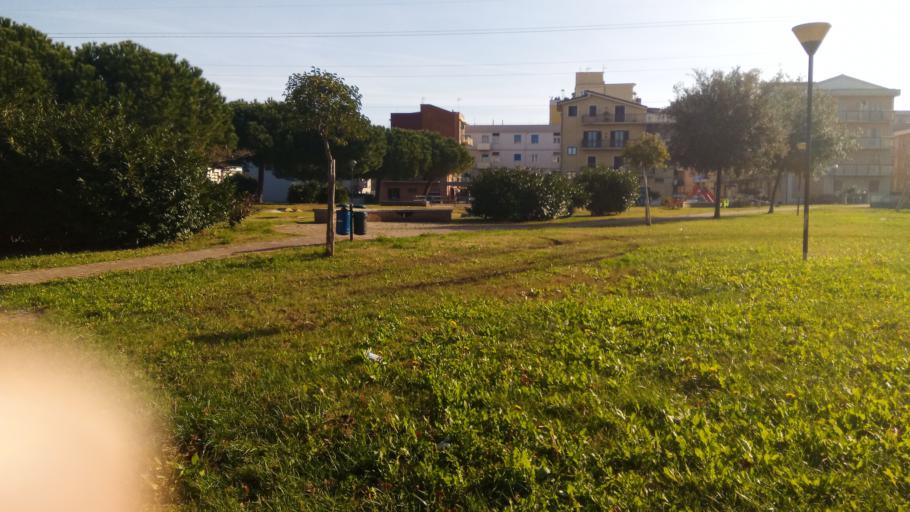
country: IT
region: Molise
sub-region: Provincia di Campobasso
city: Termoli
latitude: 42.0022
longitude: 14.9870
